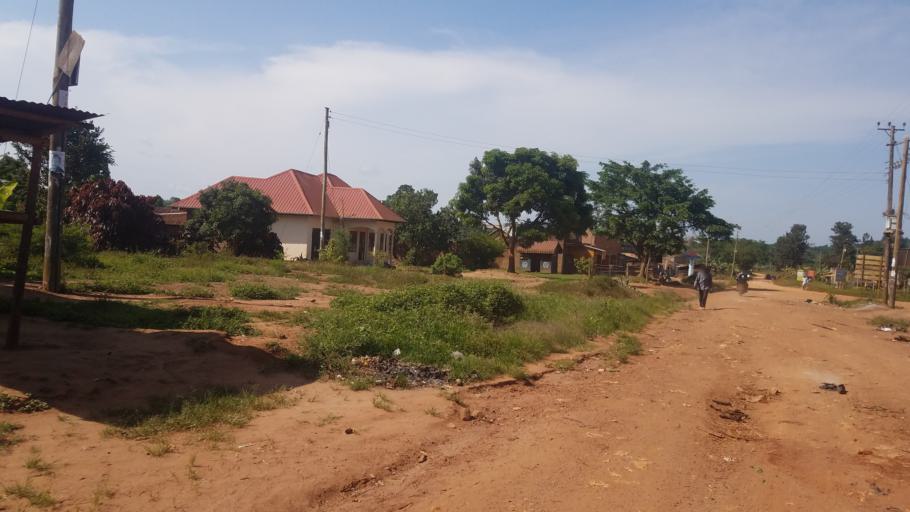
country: UG
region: Central Region
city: Masaka
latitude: -0.3125
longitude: 31.6816
